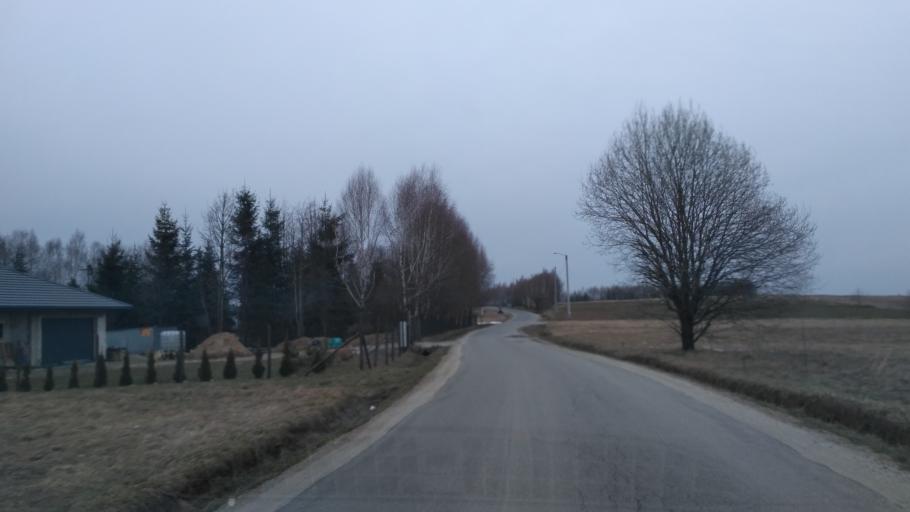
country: PL
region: Subcarpathian Voivodeship
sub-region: Powiat rzeszowski
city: Lubenia
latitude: 49.9162
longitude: 21.9156
